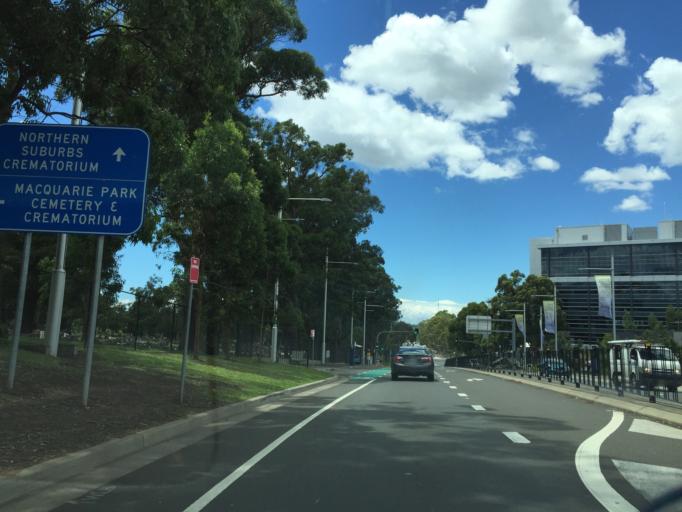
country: AU
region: New South Wales
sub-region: Ryde
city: North Ryde
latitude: -33.7943
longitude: 151.1379
